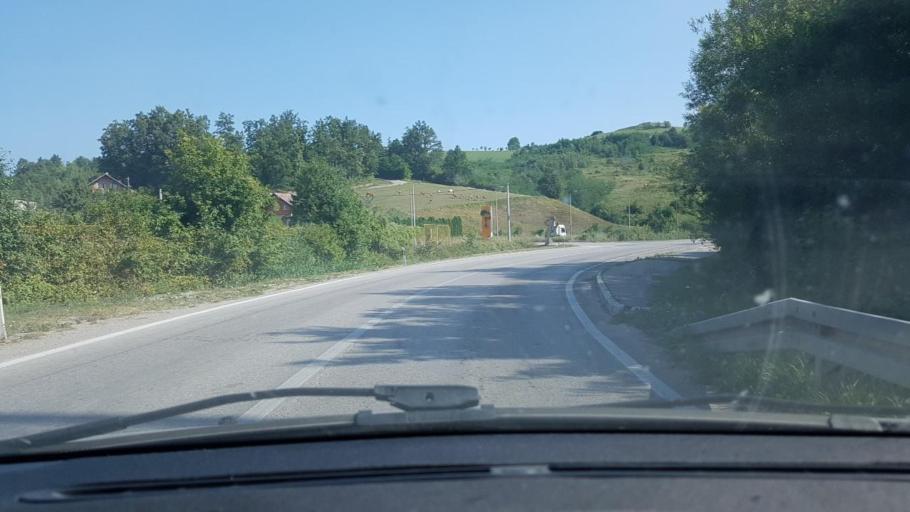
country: BA
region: Federation of Bosnia and Herzegovina
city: Coralici
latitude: 44.9954
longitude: 15.8981
